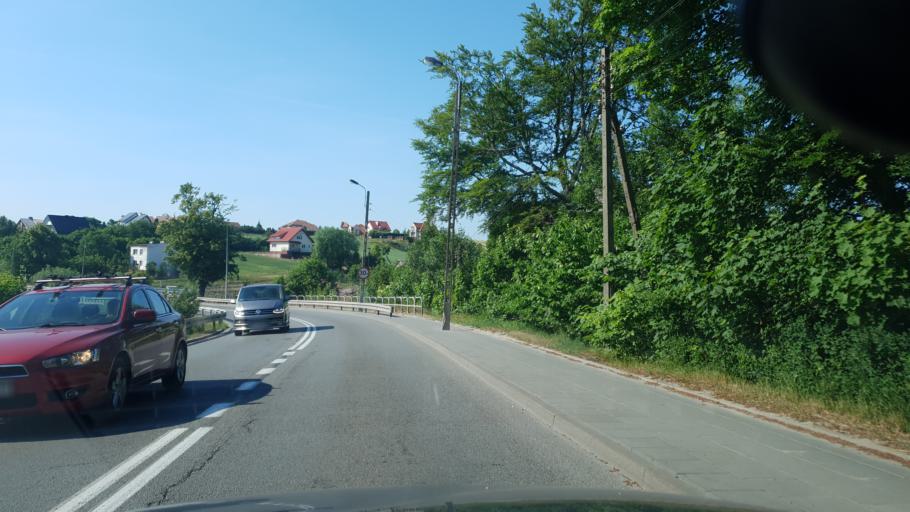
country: PL
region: Pomeranian Voivodeship
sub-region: Gdynia
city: Wielki Kack
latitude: 54.4373
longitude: 18.4628
